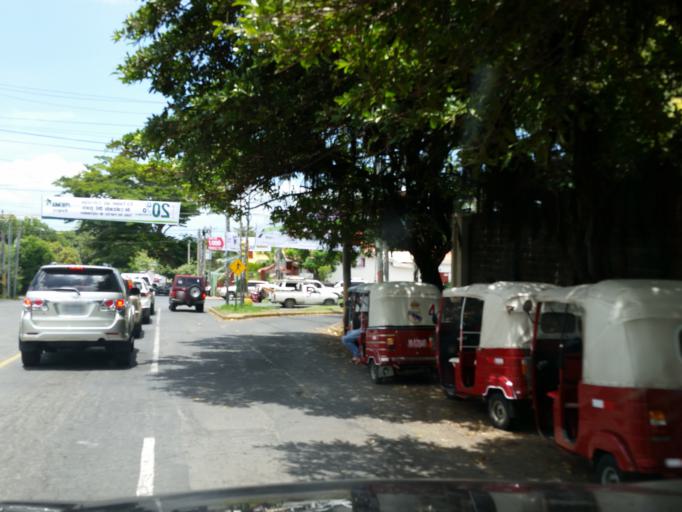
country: NI
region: Managua
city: Managua
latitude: 12.1020
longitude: -86.2626
